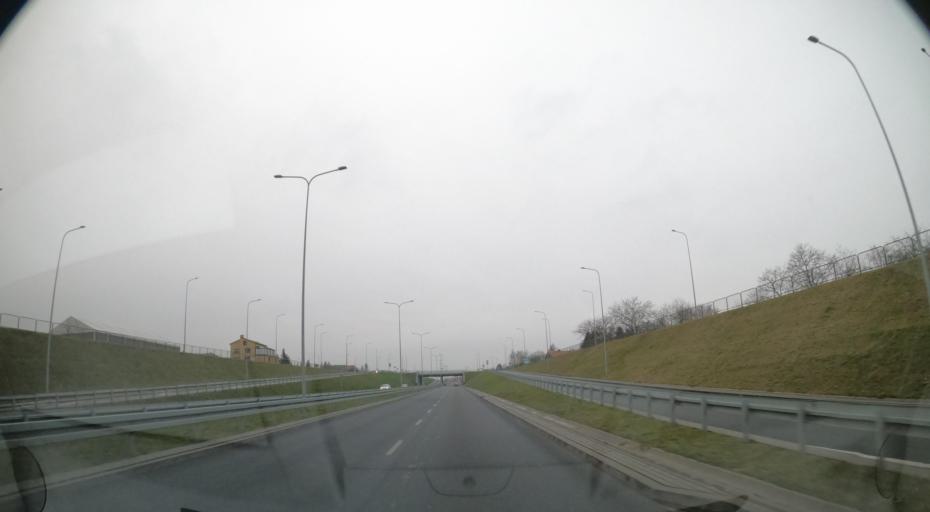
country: PL
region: Masovian Voivodeship
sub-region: Radom
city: Radom
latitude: 51.3985
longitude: 21.1982
